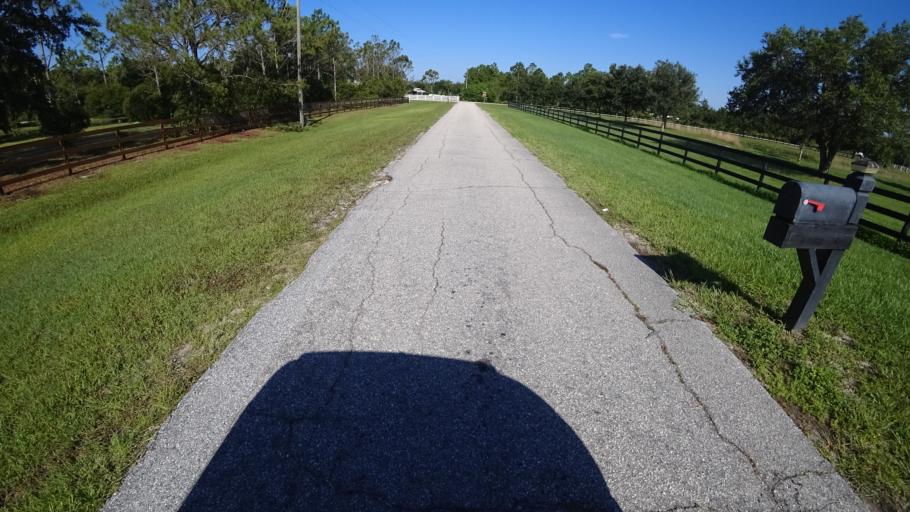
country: US
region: Florida
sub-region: Sarasota County
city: The Meadows
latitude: 27.4224
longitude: -82.3427
